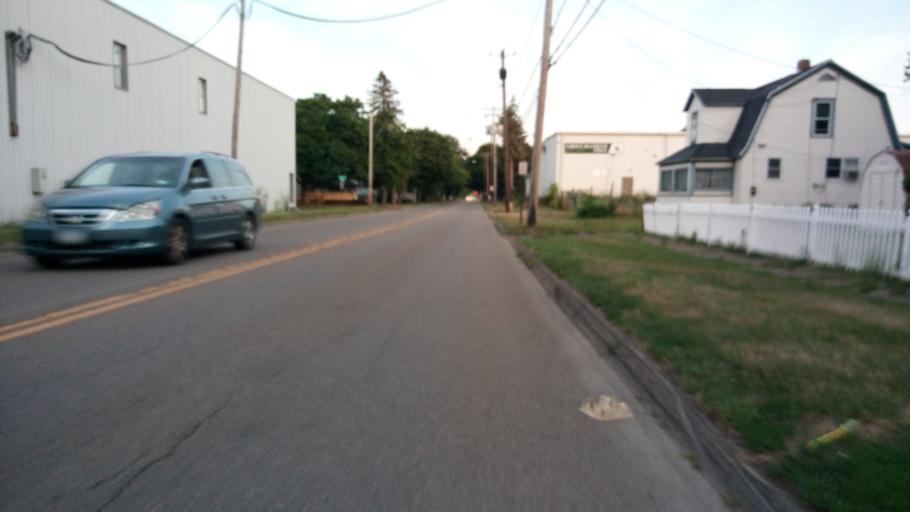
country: US
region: New York
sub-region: Chemung County
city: Elmira Heights
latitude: 42.1276
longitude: -76.8176
